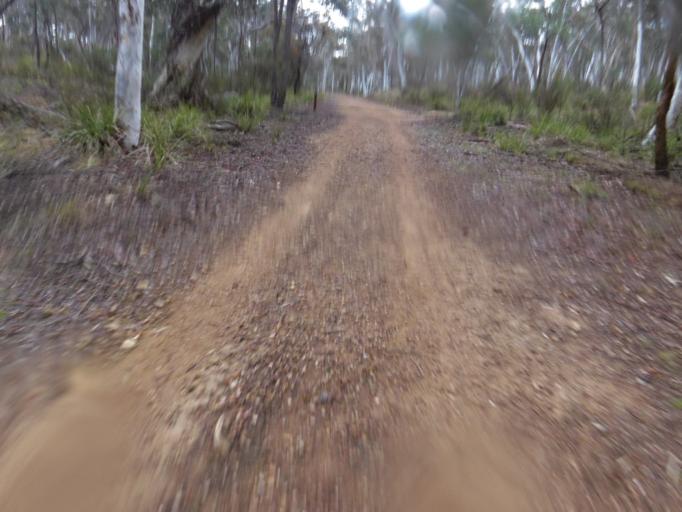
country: AU
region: Australian Capital Territory
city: Acton
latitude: -35.2661
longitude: 149.0902
